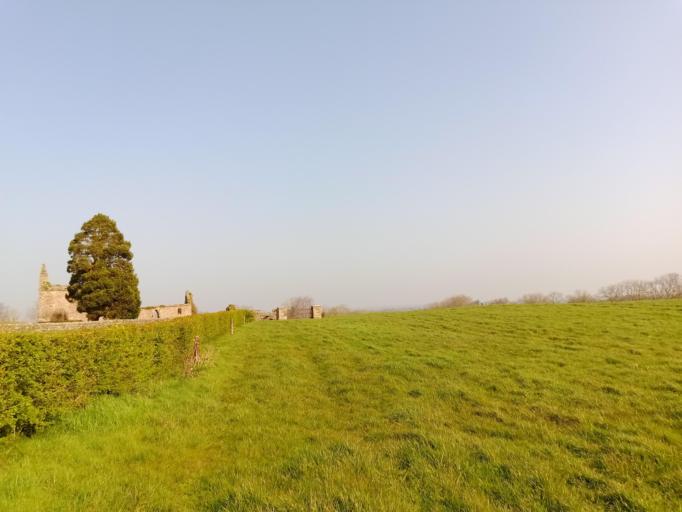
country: IE
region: Leinster
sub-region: Kilkenny
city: Callan
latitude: 52.5012
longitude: -7.3842
